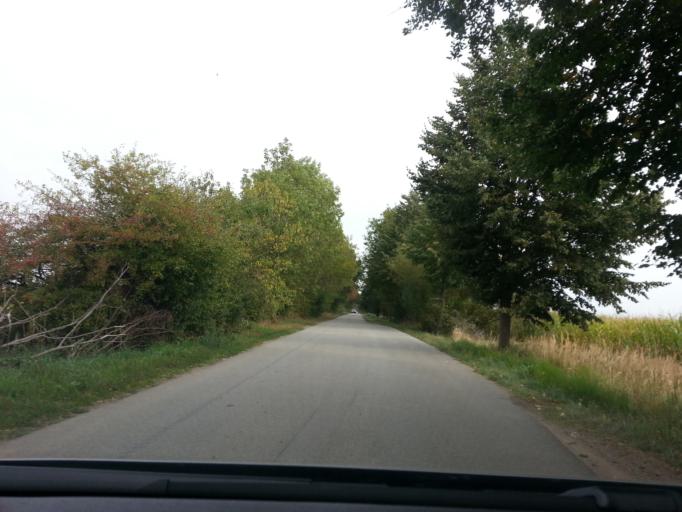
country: DE
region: Mecklenburg-Vorpommern
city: Ferdinandshof
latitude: 53.6615
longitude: 13.9177
